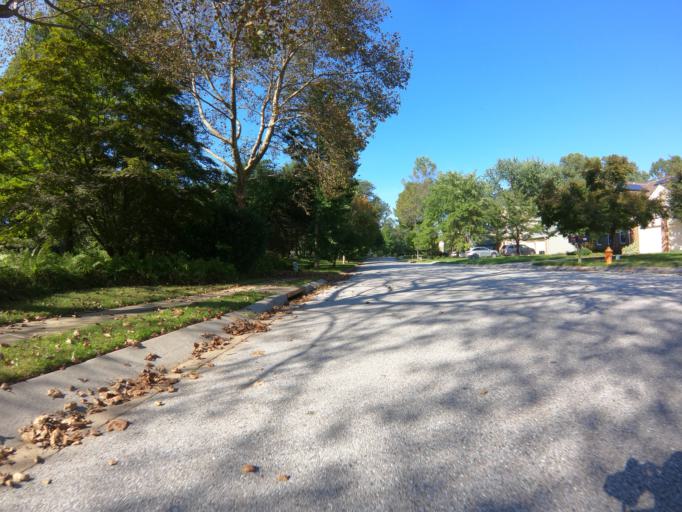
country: US
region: Maryland
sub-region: Howard County
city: Columbia
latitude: 39.2614
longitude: -76.8660
